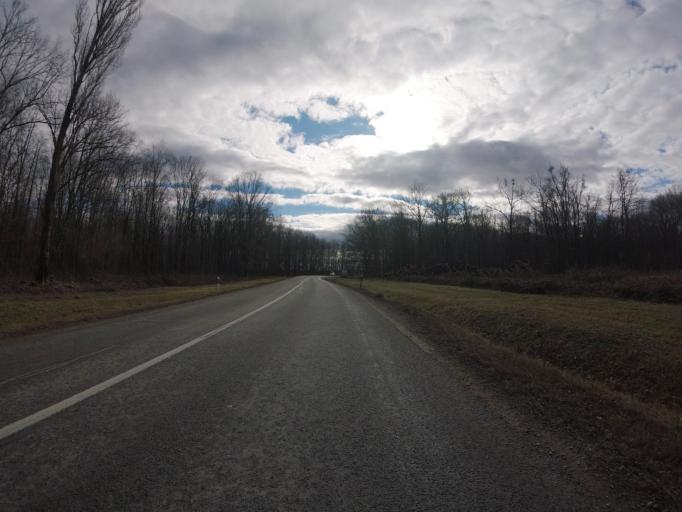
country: HR
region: Zagrebacka
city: Mraclin
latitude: 45.6543
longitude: 16.0527
